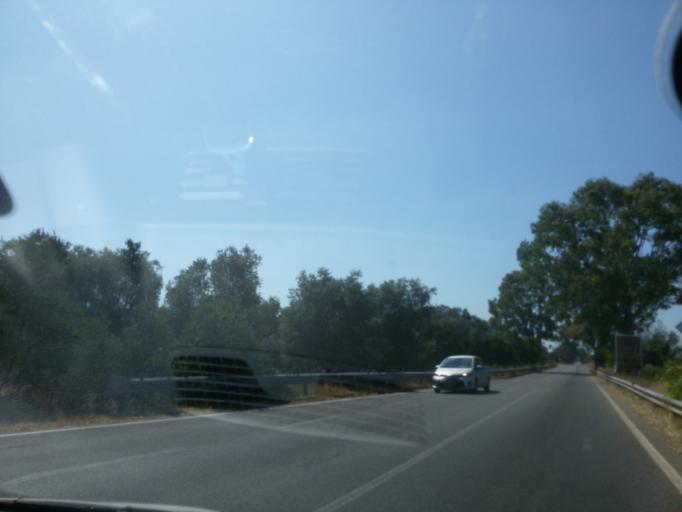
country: IT
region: Apulia
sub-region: Provincia di Lecce
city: Porto Cesareo
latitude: 40.2525
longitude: 17.9323
